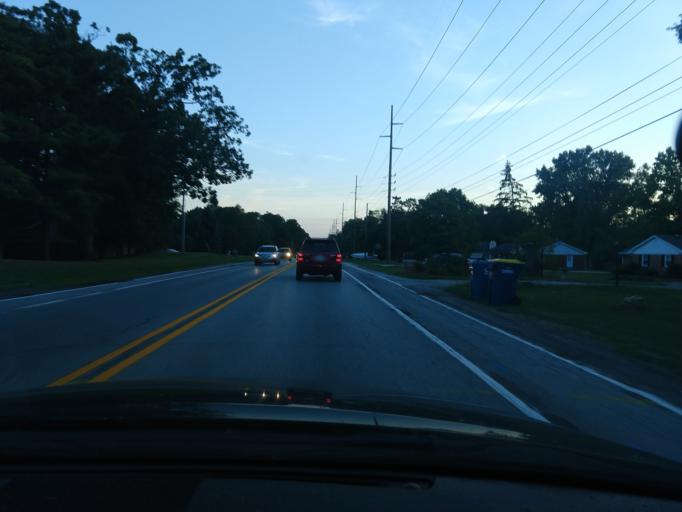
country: US
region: Indiana
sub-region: Marion County
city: Broad Ripple
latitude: 39.8953
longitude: -86.0837
